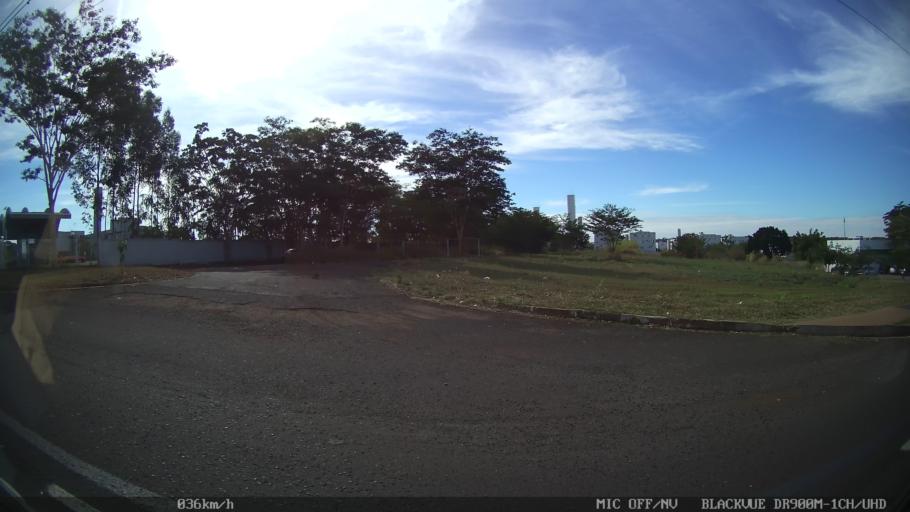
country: BR
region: Sao Paulo
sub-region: Sao Jose Do Rio Preto
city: Sao Jose do Rio Preto
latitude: -20.7998
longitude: -49.3360
